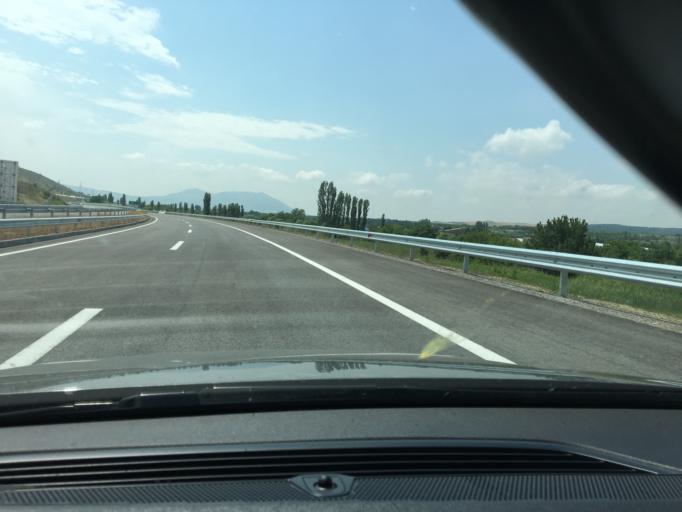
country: MK
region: Sveti Nikole
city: Sveti Nikole
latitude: 41.8623
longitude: 21.9559
